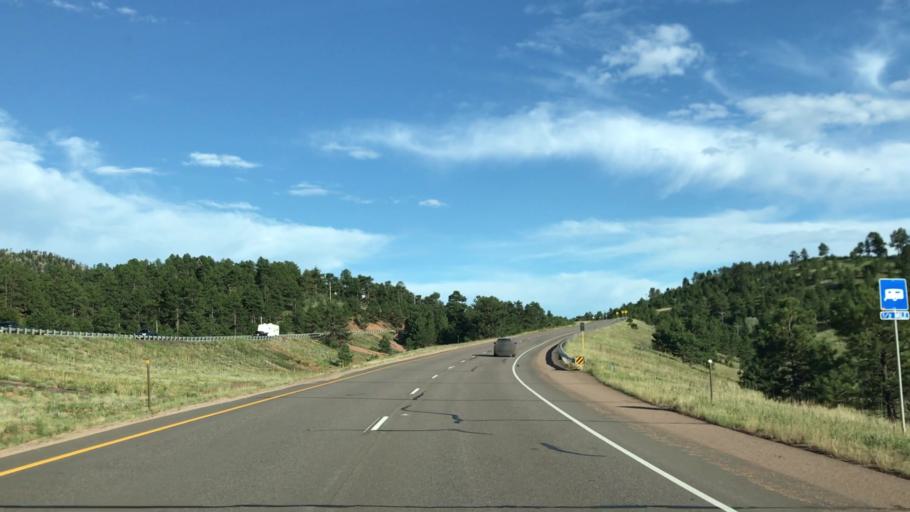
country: US
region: Colorado
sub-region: El Paso County
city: Cascade-Chipita Park
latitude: 38.9393
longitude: -105.0125
